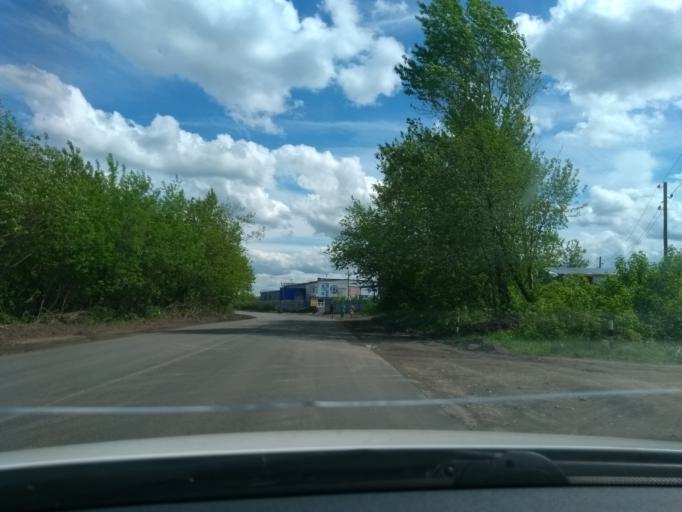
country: RU
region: Perm
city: Kondratovo
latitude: 58.0084
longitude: 56.0850
